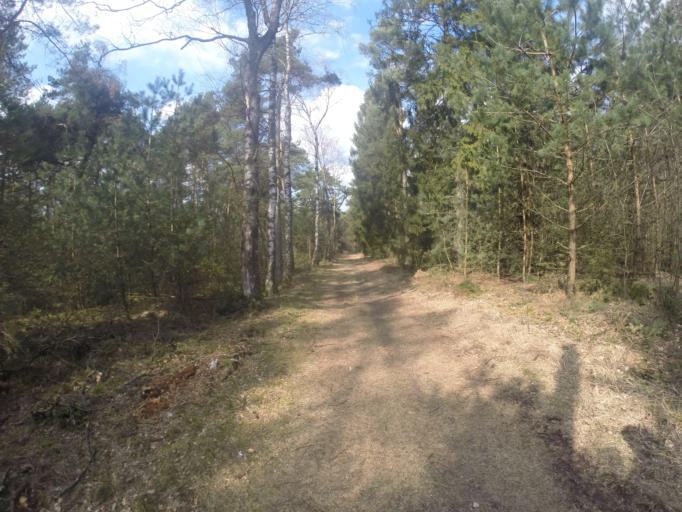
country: NL
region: Gelderland
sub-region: Gemeente Lochem
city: Almen
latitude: 52.1318
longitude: 6.3232
